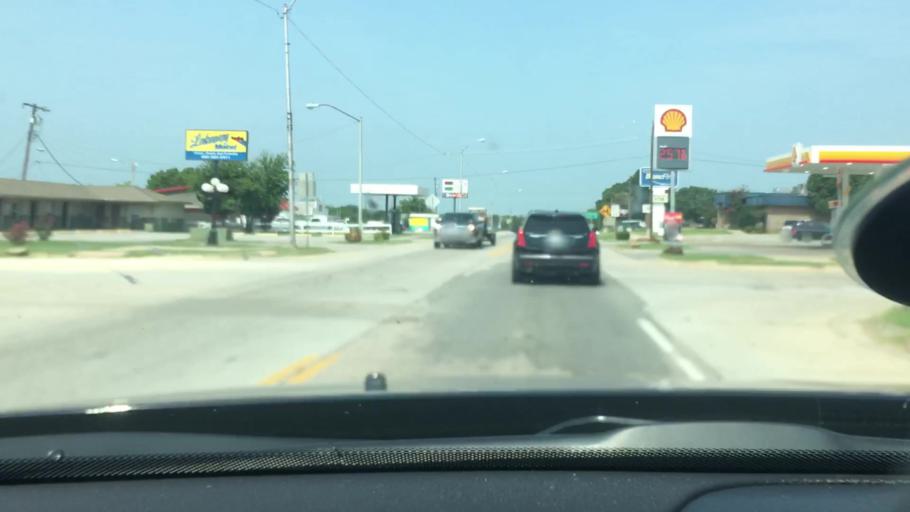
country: US
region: Oklahoma
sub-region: Marshall County
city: Kingston
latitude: 33.9986
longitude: -96.7208
